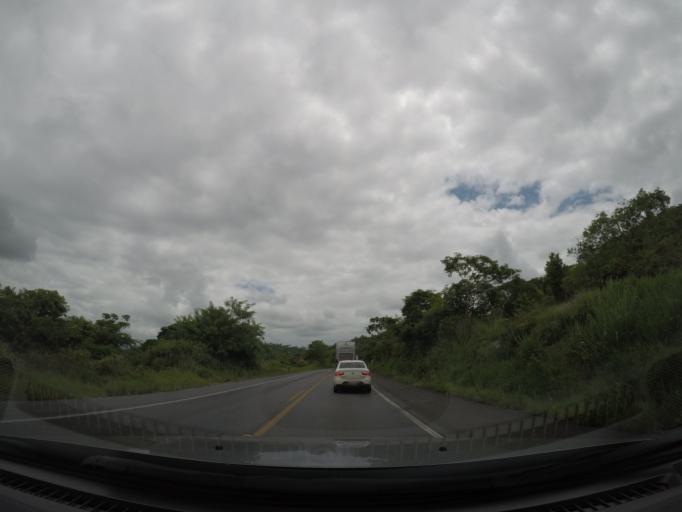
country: BR
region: Bahia
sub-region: Ruy Barbosa
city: Terra Nova
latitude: -12.4516
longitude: -40.6006
